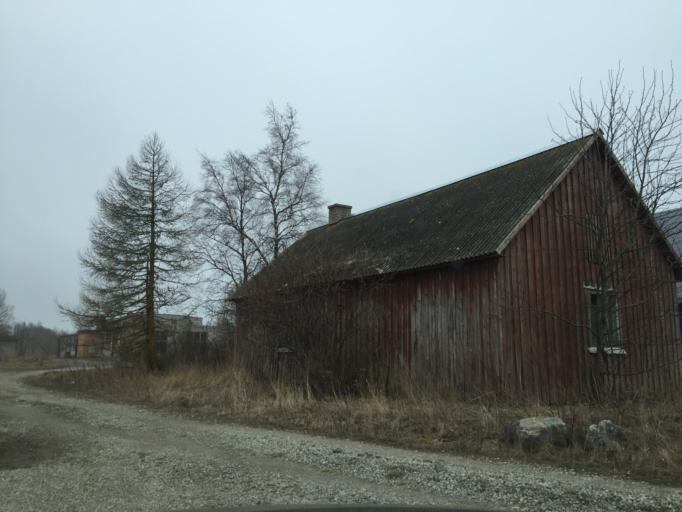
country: EE
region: Laeaene
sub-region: Lihula vald
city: Lihula
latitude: 58.5885
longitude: 23.5249
